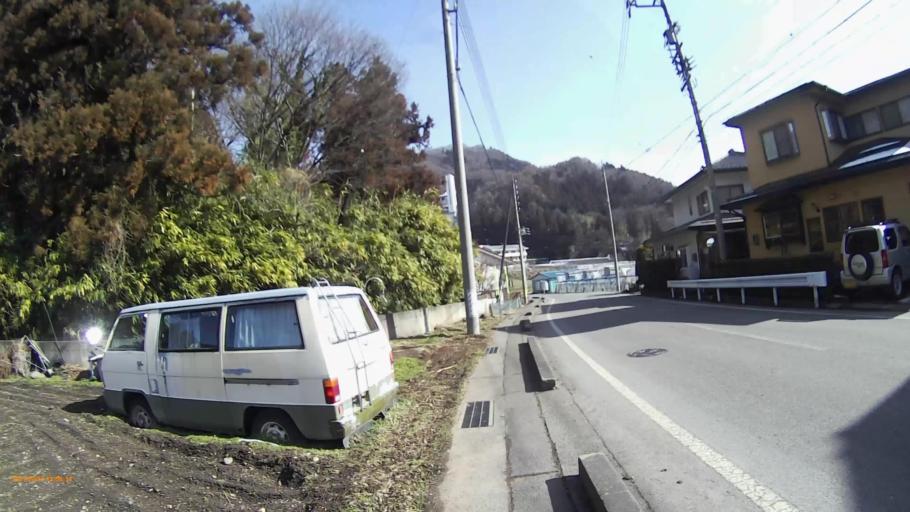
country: JP
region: Nagano
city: Nakano
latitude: 36.7476
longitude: 138.3797
